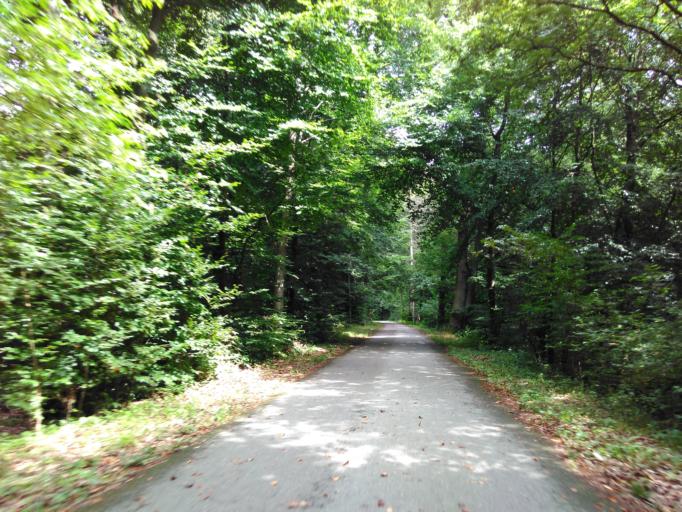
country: LU
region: Luxembourg
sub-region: Canton de Luxembourg
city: Sandweiler
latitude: 49.6470
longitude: 6.2200
